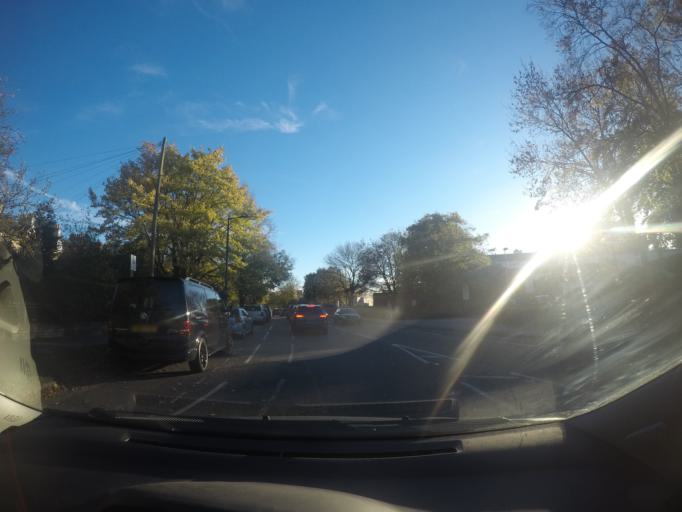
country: GB
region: England
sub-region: City of York
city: York
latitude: 53.9713
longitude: -1.0820
